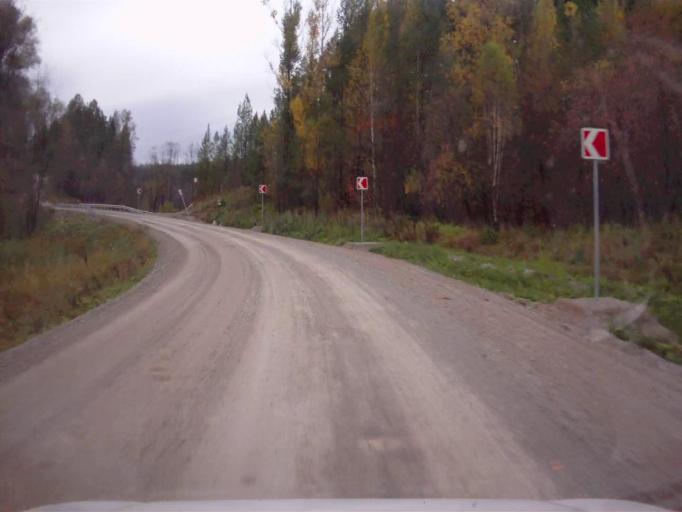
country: RU
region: Chelyabinsk
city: Nyazepetrovsk
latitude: 56.0475
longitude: 59.5023
